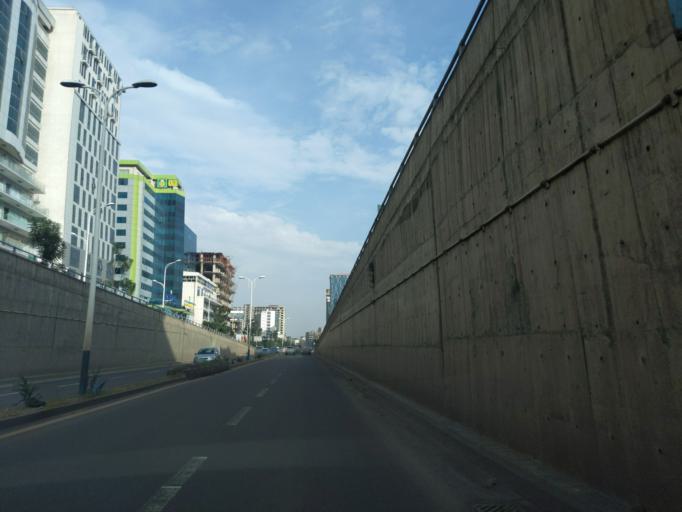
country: ET
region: Adis Abeba
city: Addis Ababa
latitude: 9.0036
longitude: 38.7684
